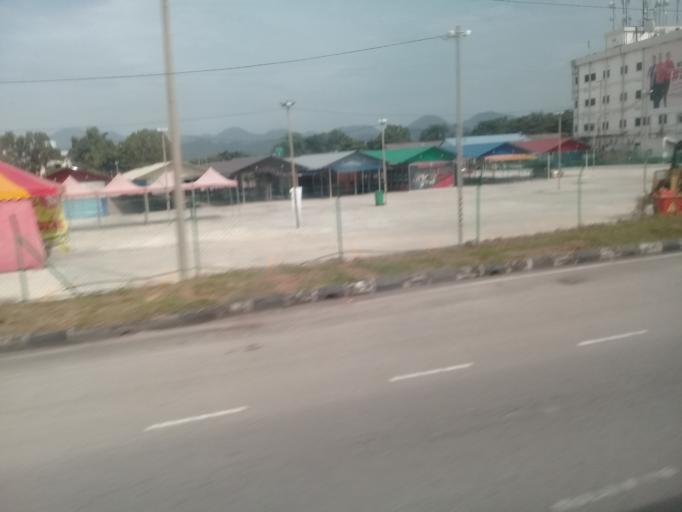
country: MY
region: Perak
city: Ipoh
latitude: 4.6148
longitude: 101.1170
